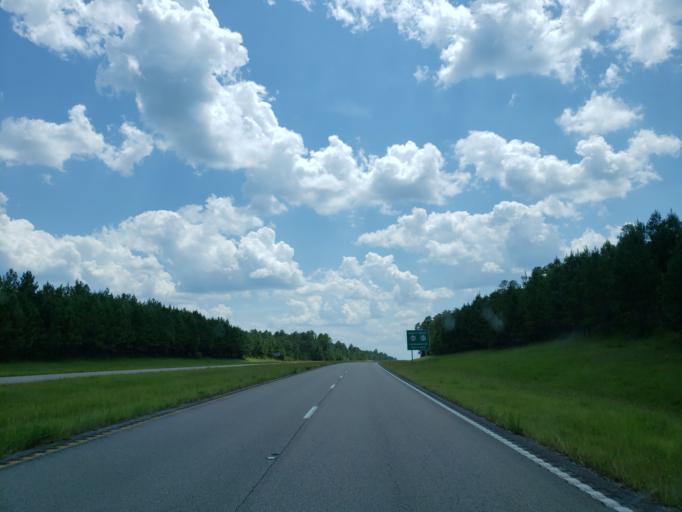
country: US
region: Mississippi
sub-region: Greene County
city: Leakesville
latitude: 31.1471
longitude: -88.5014
